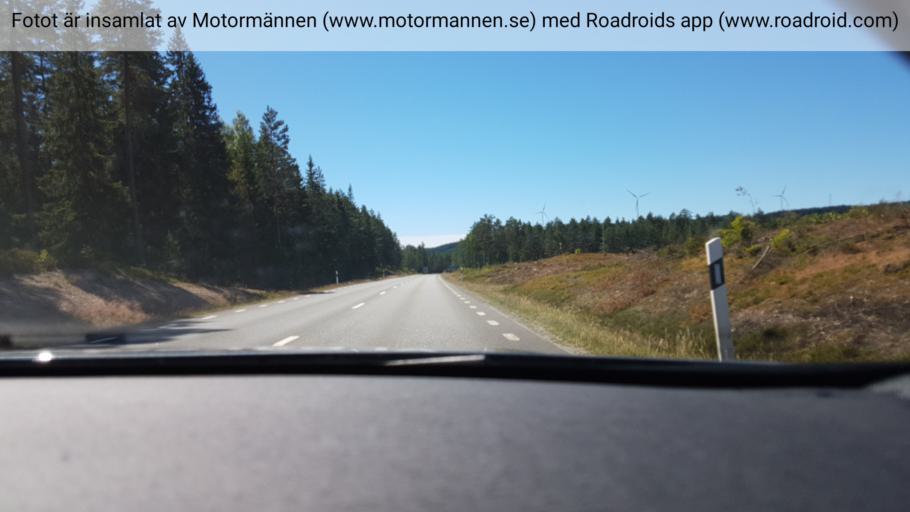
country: SE
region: Joenkoeping
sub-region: Mullsjo Kommun
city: Mullsjoe
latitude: 57.7692
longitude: 13.8325
